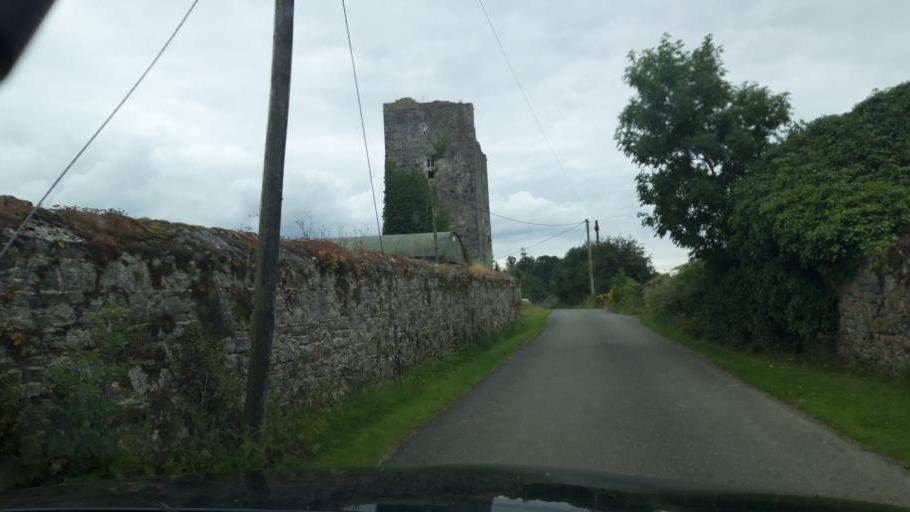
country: IE
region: Leinster
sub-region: Kilkenny
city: Thomastown
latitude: 52.6253
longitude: -7.0676
